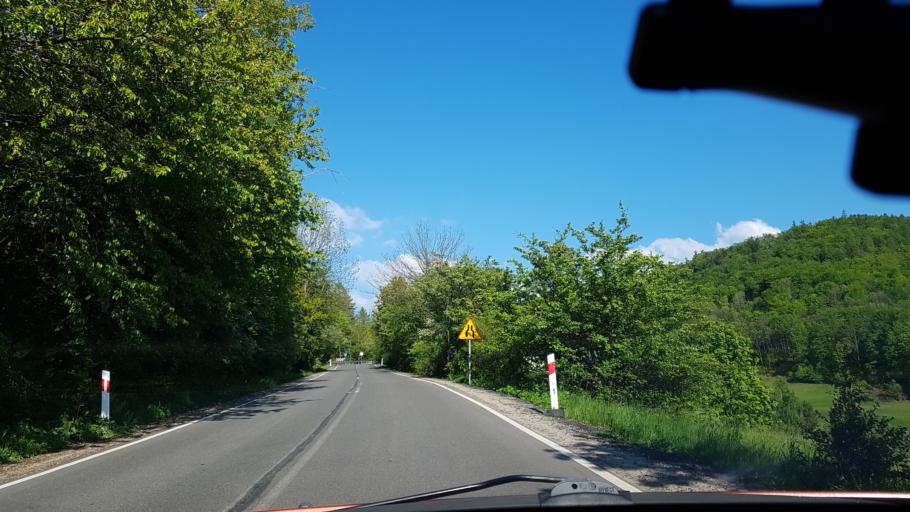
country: PL
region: Lower Silesian Voivodeship
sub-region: Powiat klodzki
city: Bozkow
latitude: 50.5709
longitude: 16.6232
